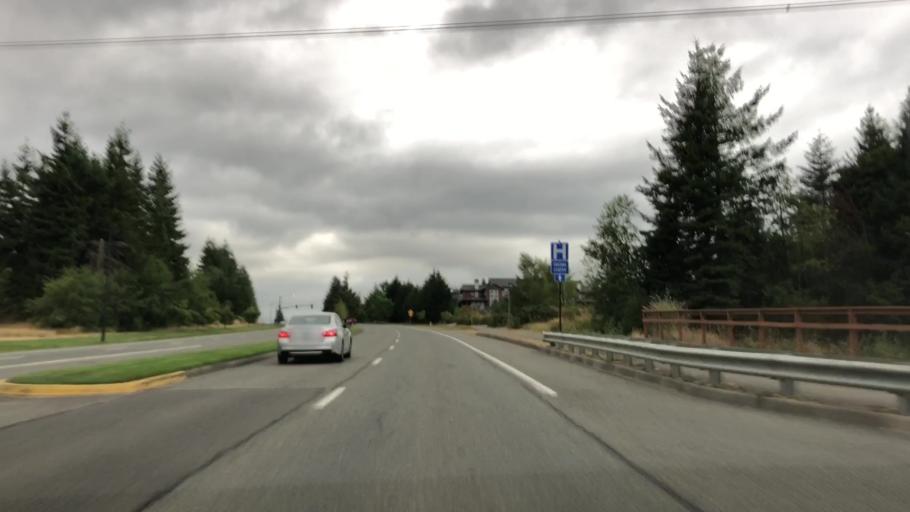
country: US
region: Washington
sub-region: King County
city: Snoqualmie
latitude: 47.5302
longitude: -121.8643
